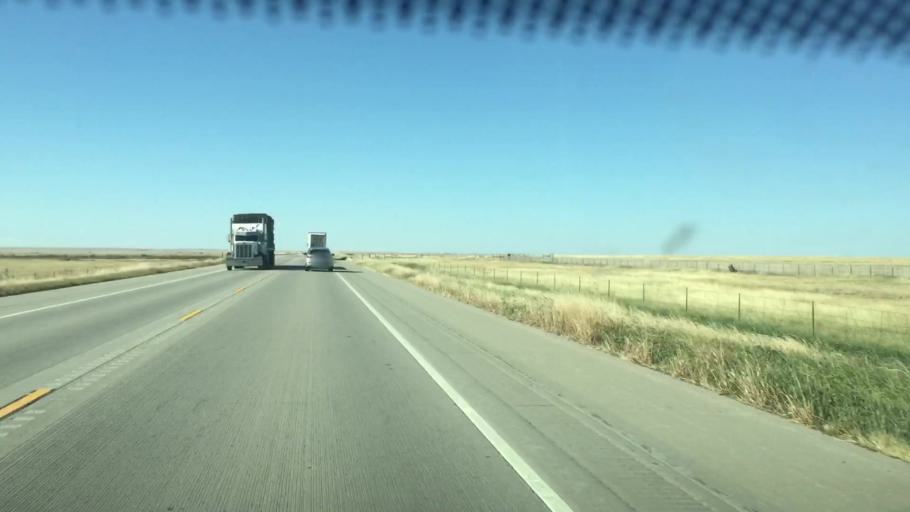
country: US
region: Colorado
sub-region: Kiowa County
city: Eads
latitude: 38.3586
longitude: -102.7185
